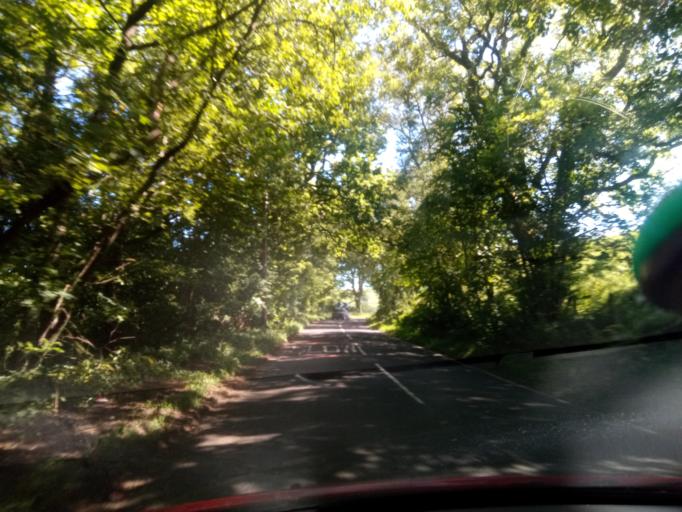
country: GB
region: England
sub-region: Northumberland
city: Bardon Mill
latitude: 54.8924
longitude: -2.3521
